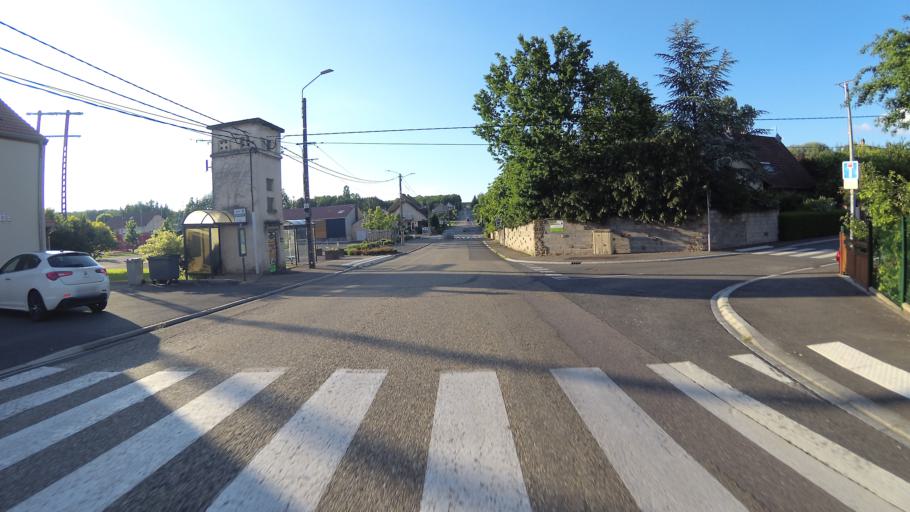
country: FR
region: Lorraine
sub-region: Departement de la Moselle
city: Remelfing
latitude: 49.0630
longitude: 7.0911
